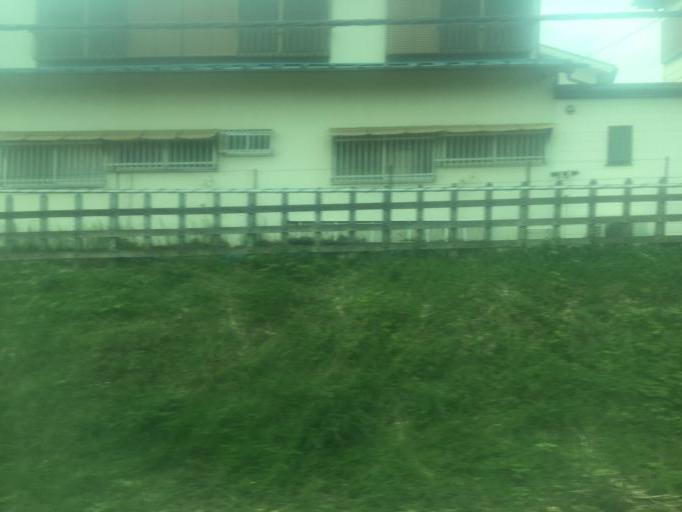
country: JP
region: Tokyo
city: Hino
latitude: 35.6883
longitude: 139.4260
